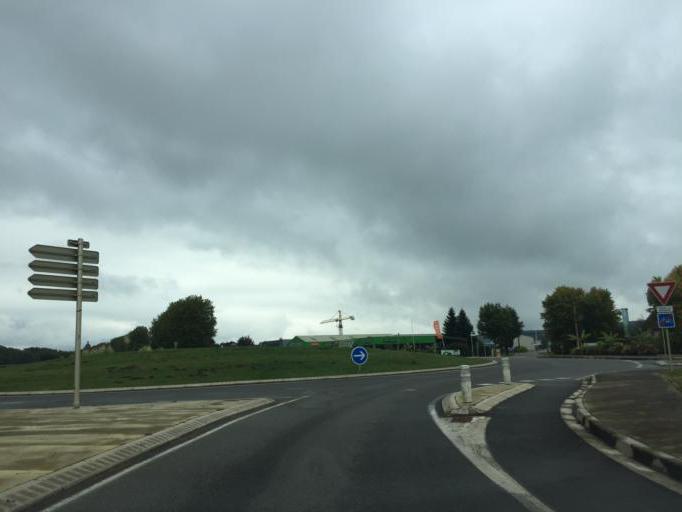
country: FR
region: Franche-Comte
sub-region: Departement du Jura
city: Orgelet
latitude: 46.5344
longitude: 5.6047
